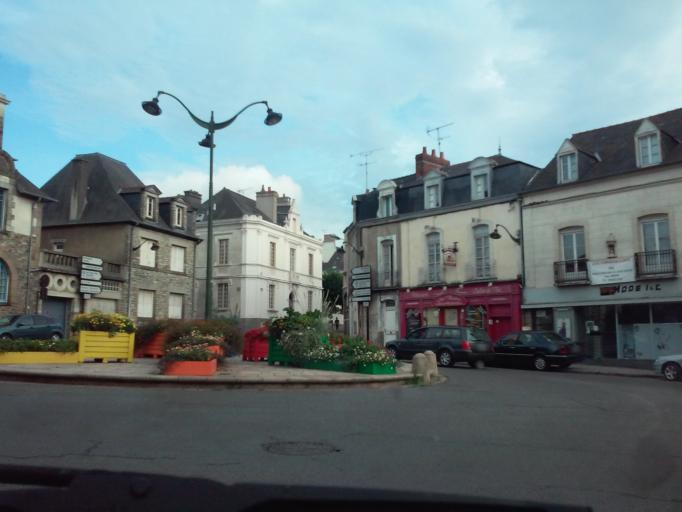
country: FR
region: Brittany
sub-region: Departement d'Ille-et-Vilaine
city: Vitre
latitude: 48.1233
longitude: -1.2101
